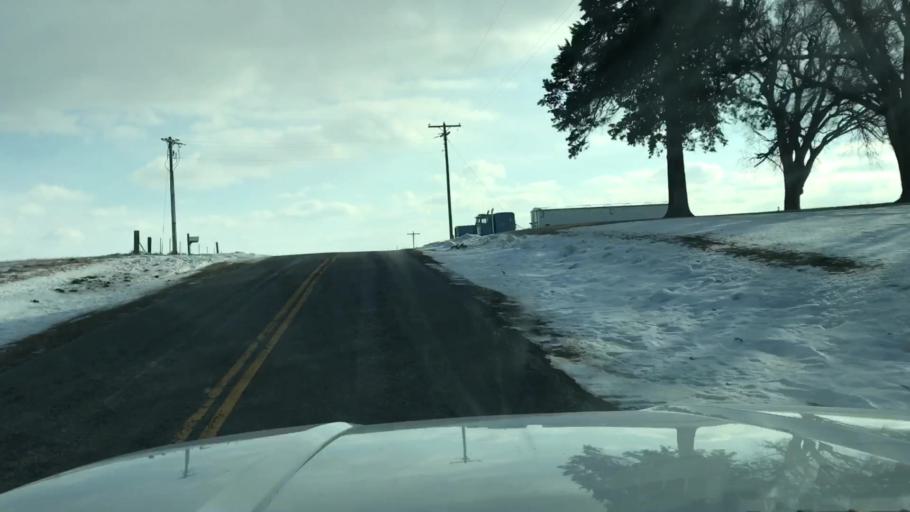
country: US
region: Missouri
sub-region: Nodaway County
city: Maryville
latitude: 40.1884
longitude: -95.0122
